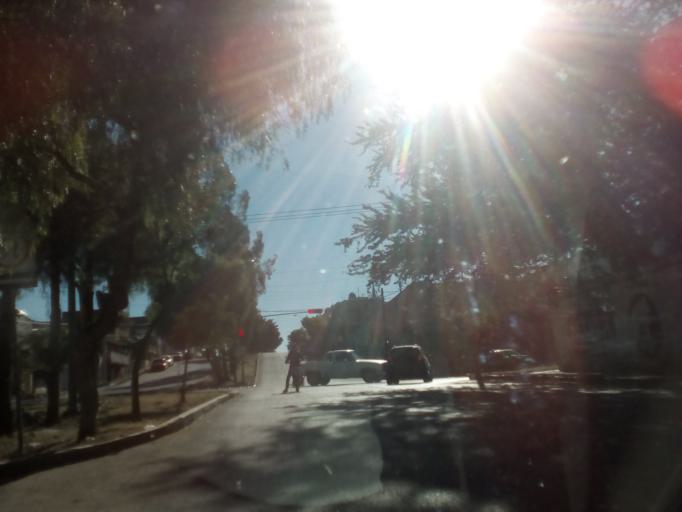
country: MX
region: Guanajuato
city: Leon
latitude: 21.1258
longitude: -101.6974
